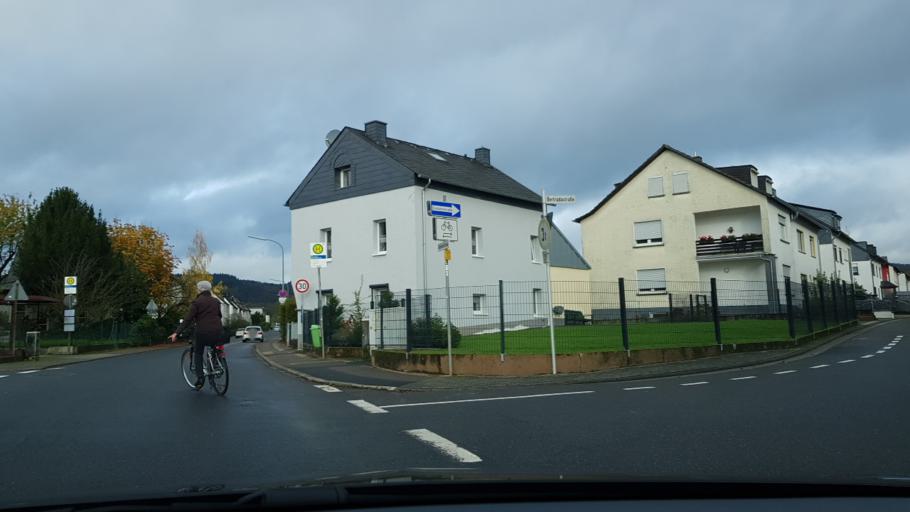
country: DE
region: Rheinland-Pfalz
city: Schweich
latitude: 49.8248
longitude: 6.7479
